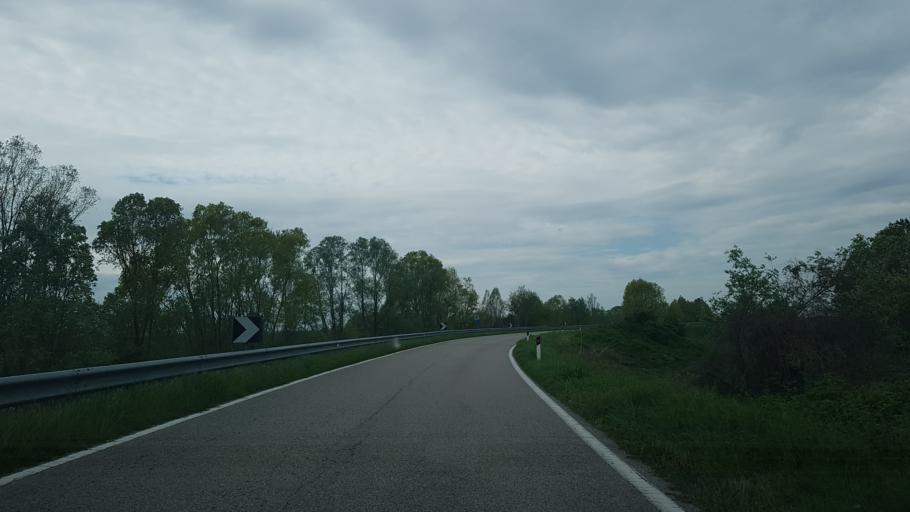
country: IT
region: Veneto
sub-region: Provincia di Padova
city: Barbona
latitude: 45.0993
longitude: 11.6951
